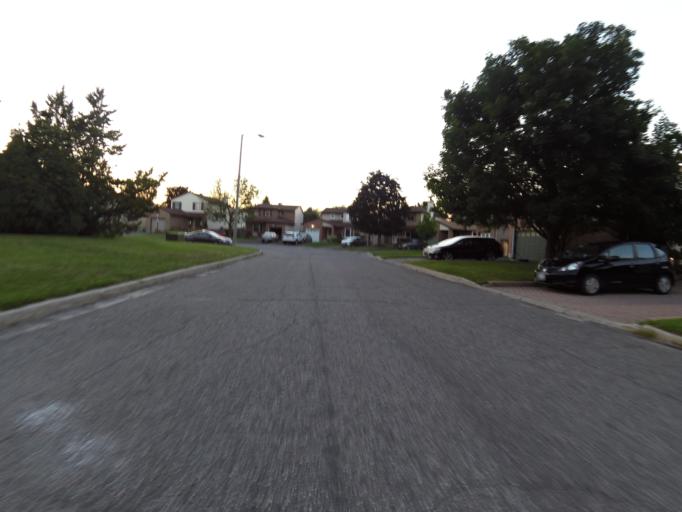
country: CA
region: Quebec
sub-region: Outaouais
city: Gatineau
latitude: 45.4649
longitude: -75.4983
